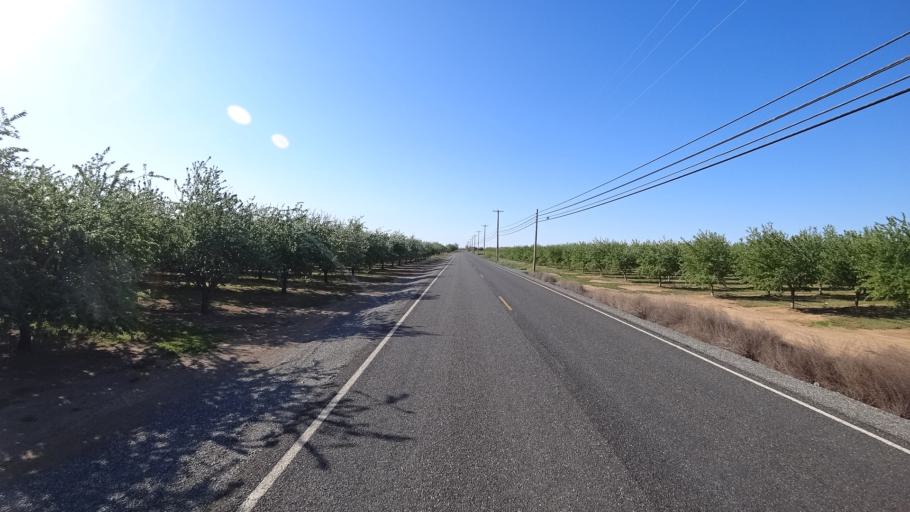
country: US
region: California
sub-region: Glenn County
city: Hamilton City
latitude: 39.7739
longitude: -122.1042
